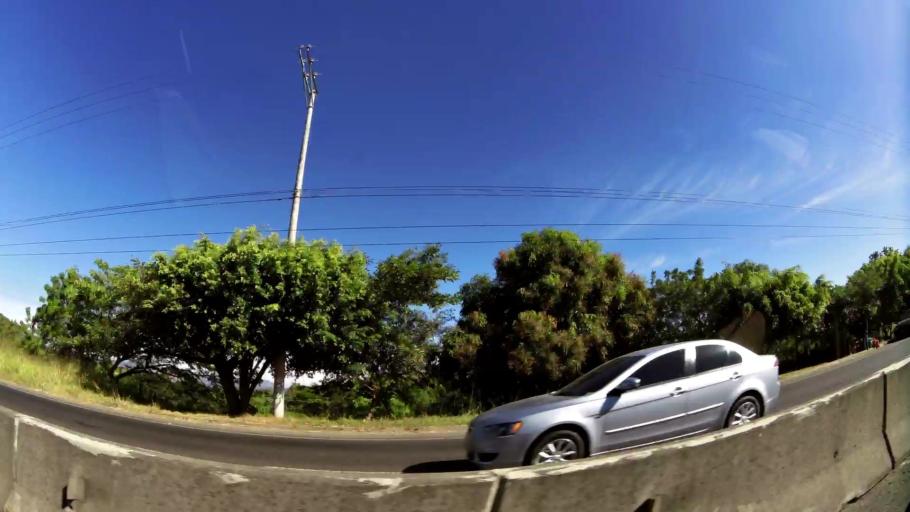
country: SV
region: Santa Ana
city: Coatepeque
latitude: 13.9392
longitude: -89.5317
